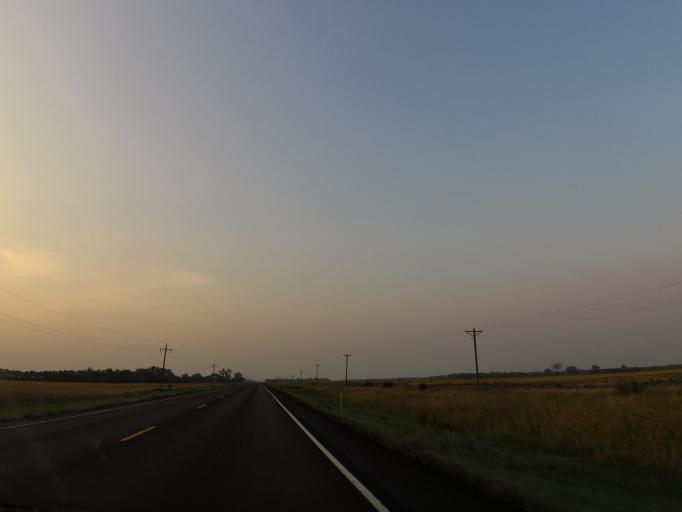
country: US
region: North Dakota
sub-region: Walsh County
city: Park River
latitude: 48.2600
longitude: -97.6225
